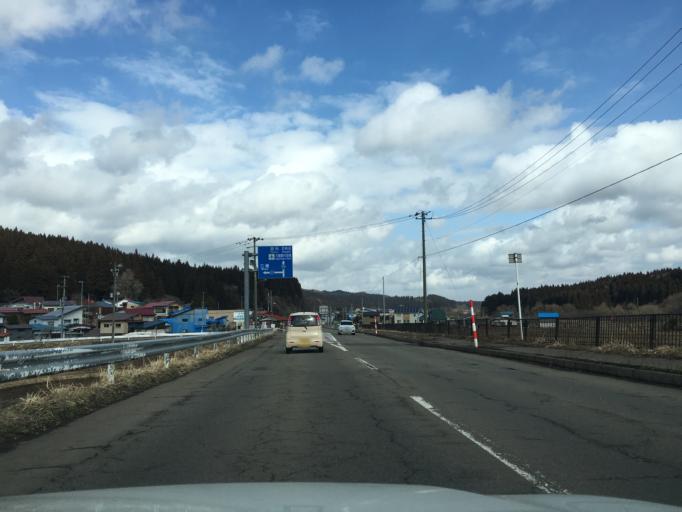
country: JP
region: Akita
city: Takanosu
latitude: 40.0310
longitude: 140.2745
